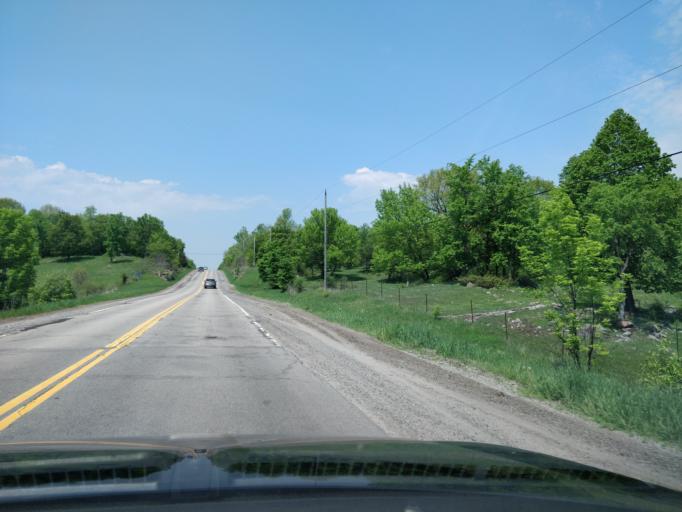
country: CA
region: Ontario
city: Perth
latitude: 44.7444
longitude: -76.3891
